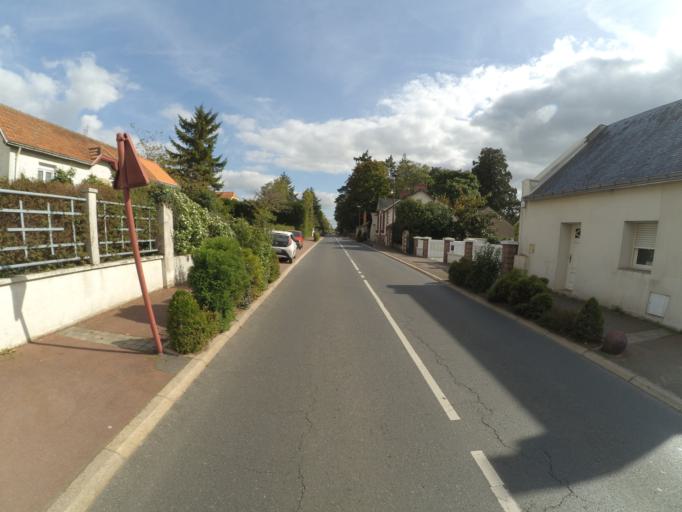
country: FR
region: Pays de la Loire
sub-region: Departement de la Loire-Atlantique
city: Suce-sur-Erdre
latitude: 47.3366
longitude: -1.5242
